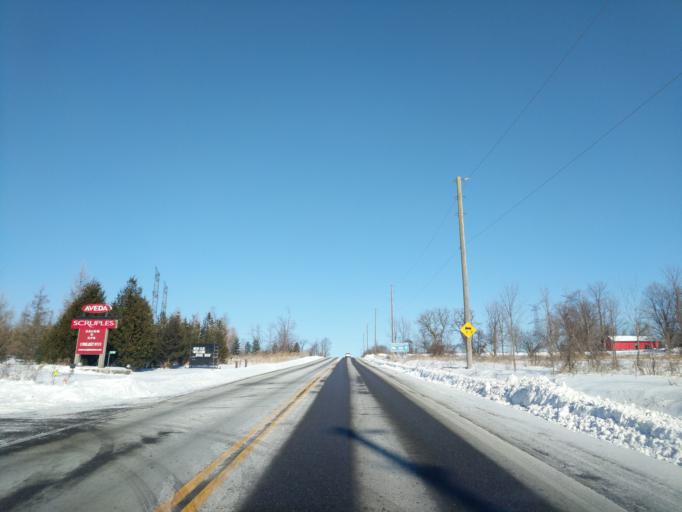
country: CA
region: Ontario
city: Pickering
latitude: 43.8495
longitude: -79.1290
